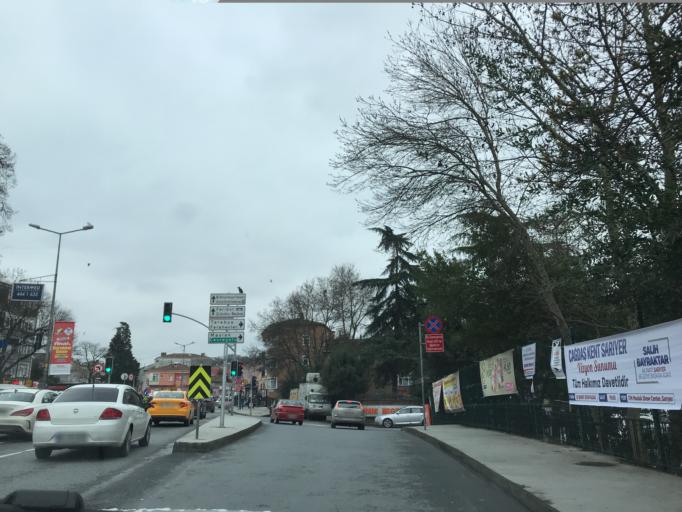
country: TR
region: Istanbul
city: Sisli
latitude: 41.1165
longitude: 29.0503
